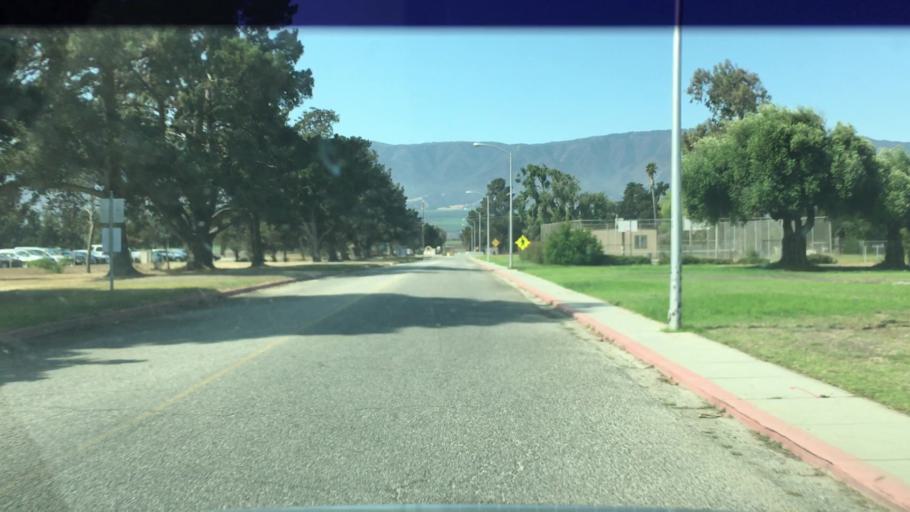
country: US
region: California
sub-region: Monterey County
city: Gonzales
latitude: 36.4680
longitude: -121.3845
